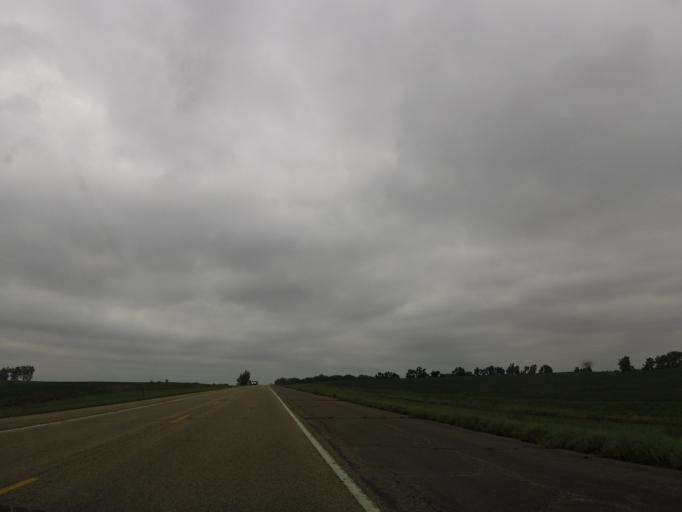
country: US
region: South Dakota
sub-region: Deuel County
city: Clear Lake
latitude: 44.9333
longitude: -96.6217
